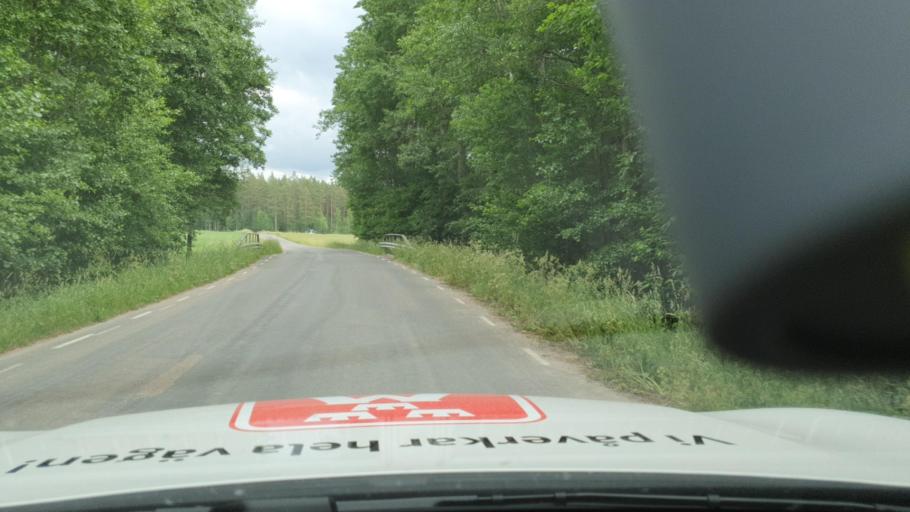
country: SE
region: Vaestra Goetaland
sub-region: Tidaholms Kommun
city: Olofstorp
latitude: 58.1927
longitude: 14.0324
